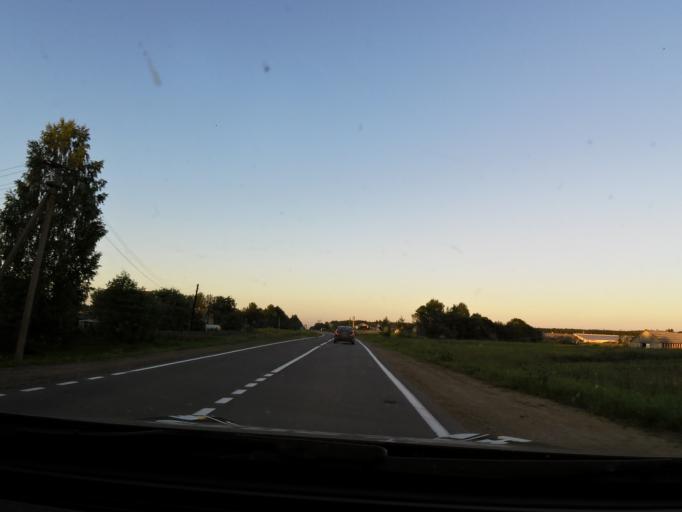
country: RU
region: Jaroslavl
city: Lyubim
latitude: 58.3588
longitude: 40.5485
